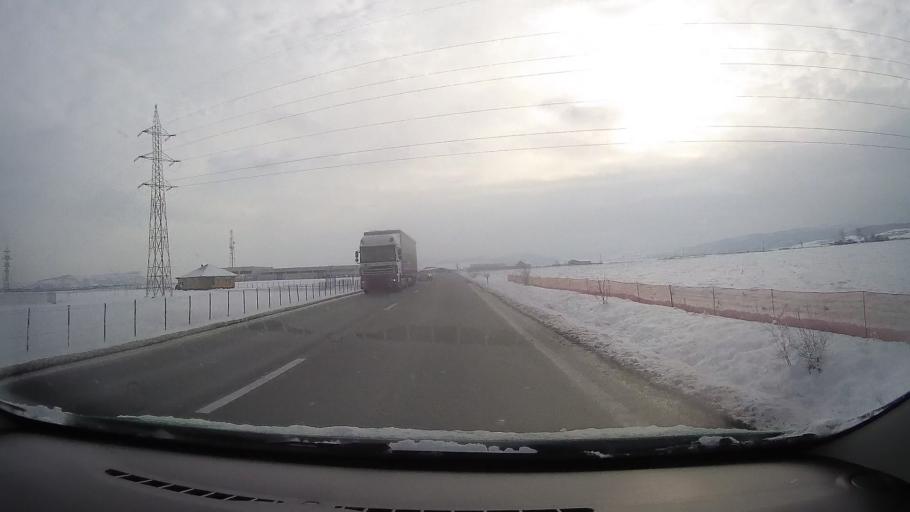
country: RO
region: Alba
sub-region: Municipiul Sebes
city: Lancram
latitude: 45.9645
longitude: 23.5323
